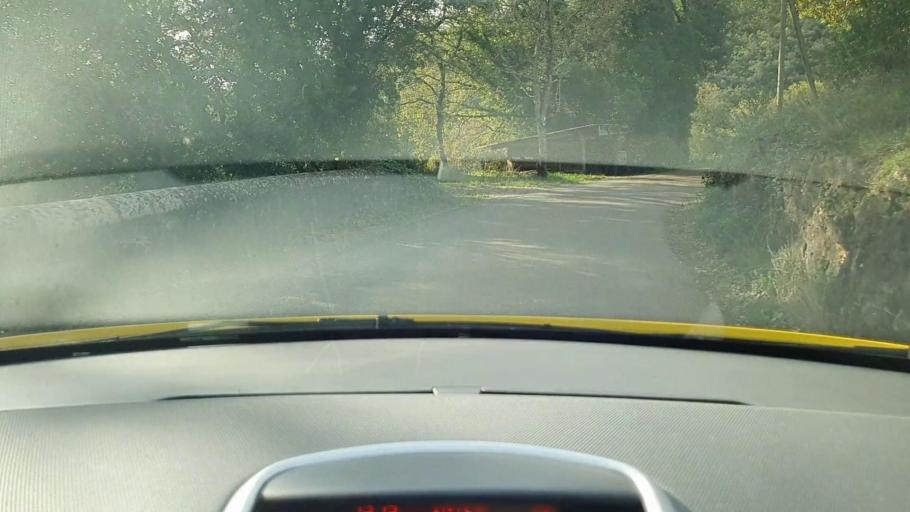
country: FR
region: Languedoc-Roussillon
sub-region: Departement du Gard
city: Anduze
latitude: 44.0508
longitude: 3.9235
